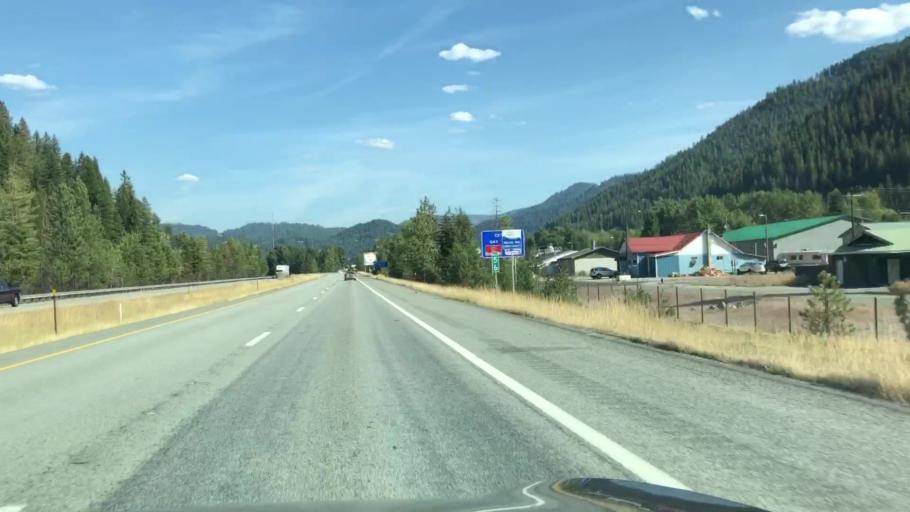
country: US
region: Idaho
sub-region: Shoshone County
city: Osburn
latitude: 47.5118
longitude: -116.0192
